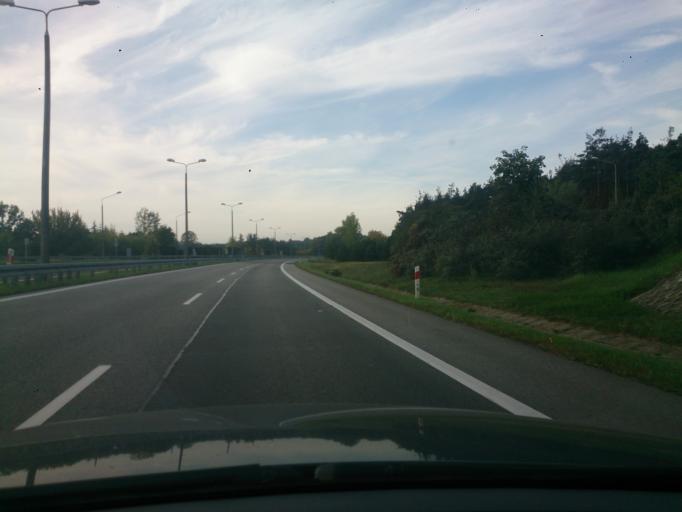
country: PL
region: Kujawsko-Pomorskie
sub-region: Powiat chelminski
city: Chelmno
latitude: 53.3796
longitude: 18.3459
